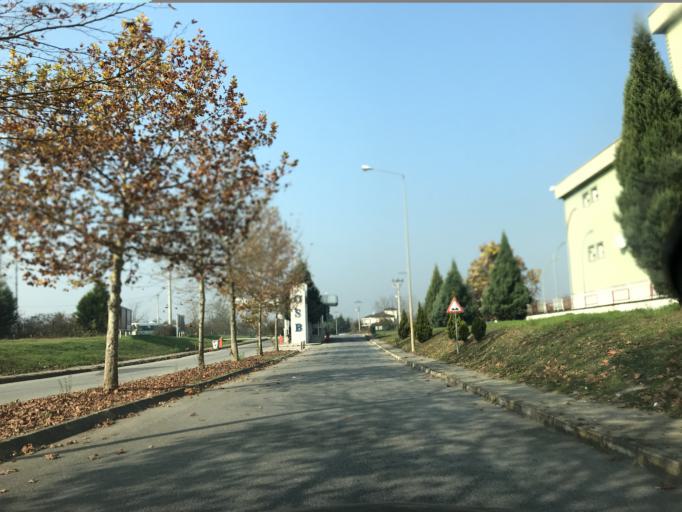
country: TR
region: Duzce
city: Duzce
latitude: 40.7890
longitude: 31.1319
